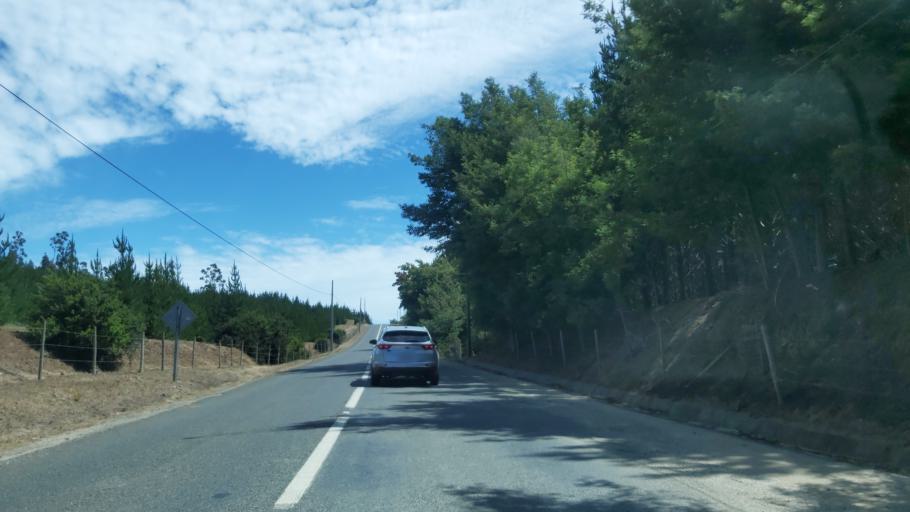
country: CL
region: Maule
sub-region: Provincia de Talca
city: Constitucion
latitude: -35.5218
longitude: -72.5355
